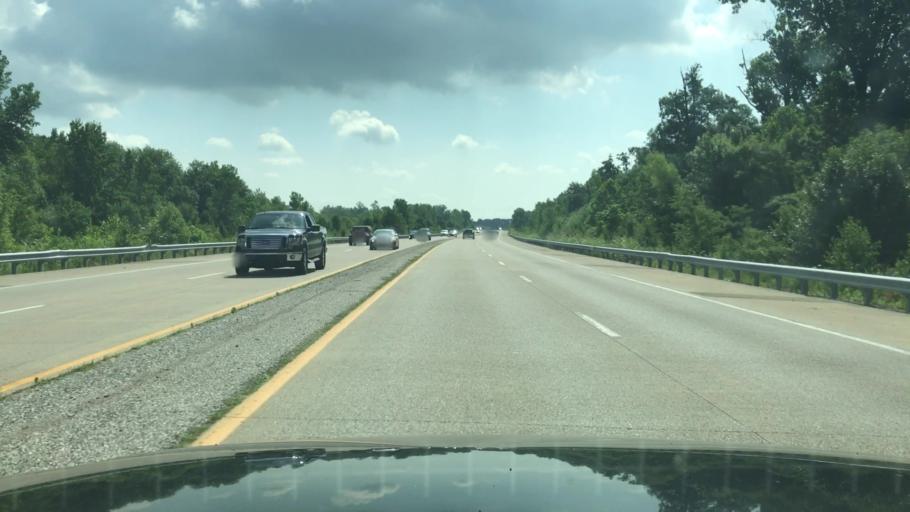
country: US
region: Indiana
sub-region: Vanderburgh County
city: Melody Hill
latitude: 38.0131
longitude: -87.5026
